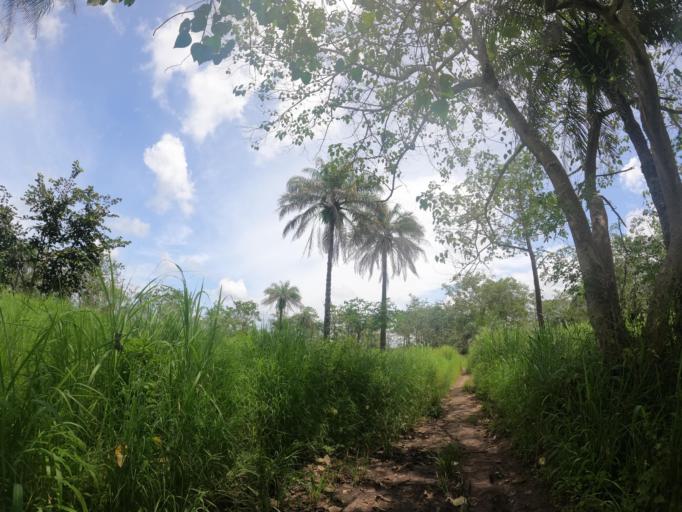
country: SL
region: Northern Province
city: Makeni
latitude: 9.1278
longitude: -12.2619
